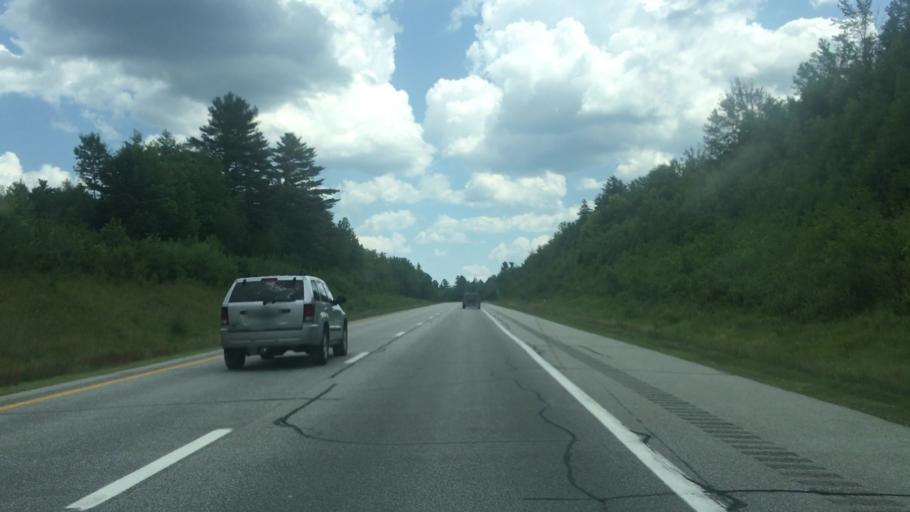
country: US
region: New Hampshire
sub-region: Merrimack County
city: New London
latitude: 43.4011
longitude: -72.0169
